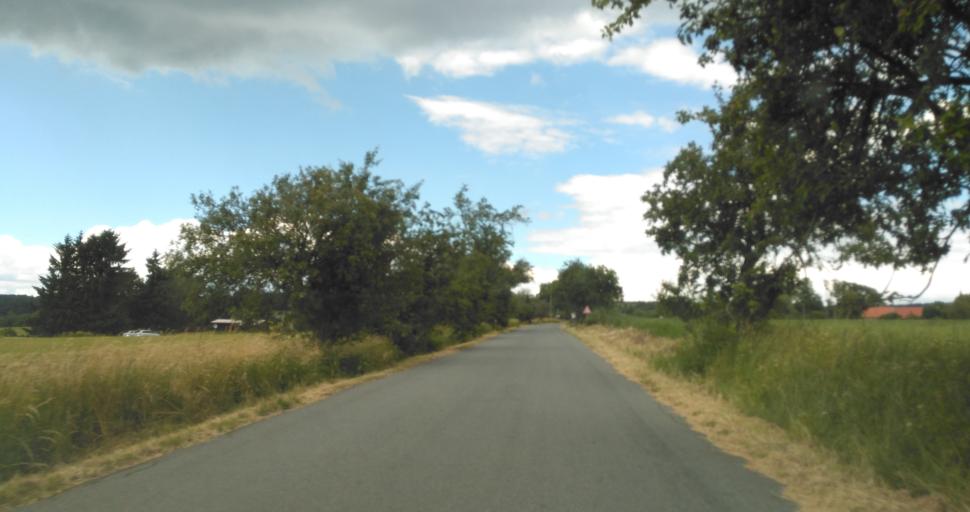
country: CZ
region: Plzensky
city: Zbiroh
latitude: 49.8804
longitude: 13.8000
